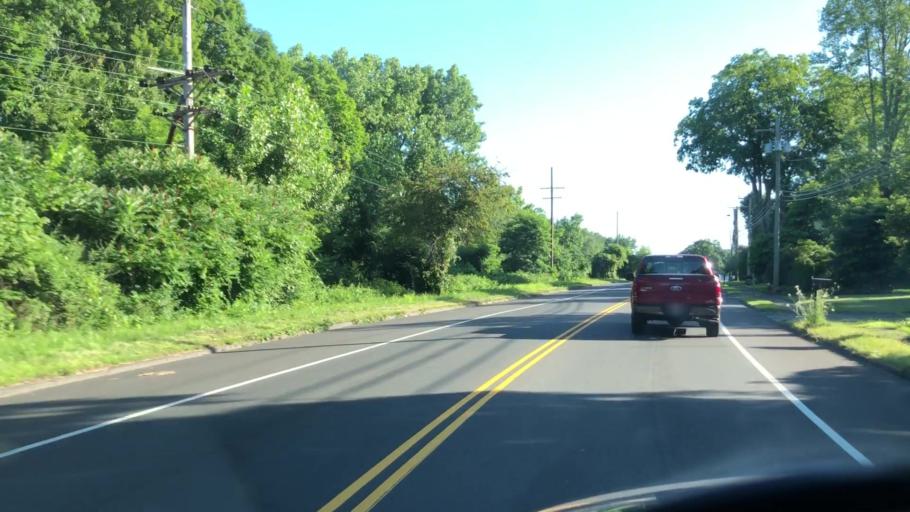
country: US
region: Massachusetts
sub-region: Hampshire County
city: Easthampton
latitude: 42.2778
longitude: -72.6554
